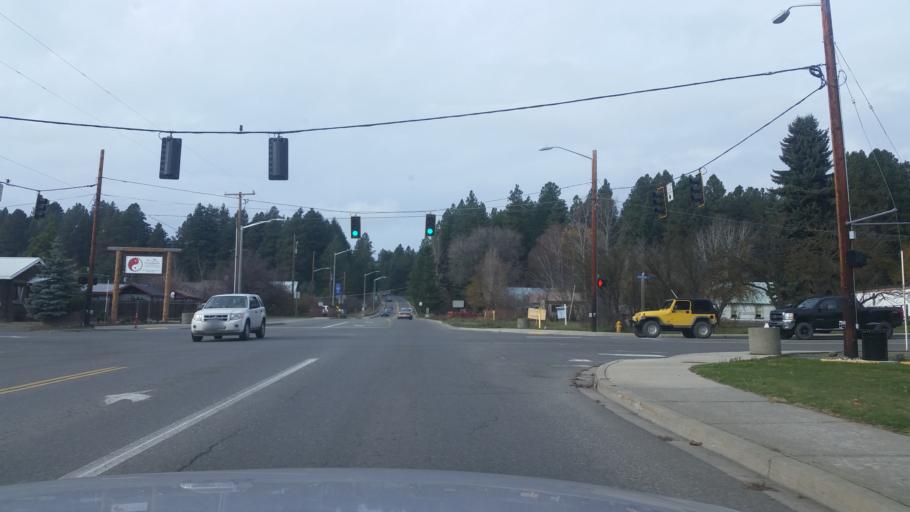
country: US
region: Washington
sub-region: Kittitas County
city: Cle Elum
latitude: 47.1956
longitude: -120.9441
